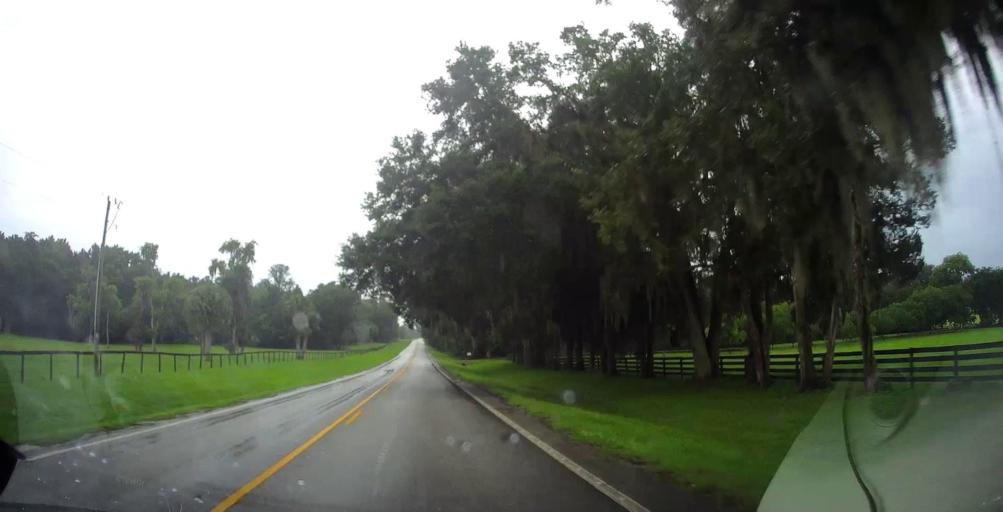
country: US
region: Florida
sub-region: Marion County
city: Citra
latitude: 29.3848
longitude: -82.2517
